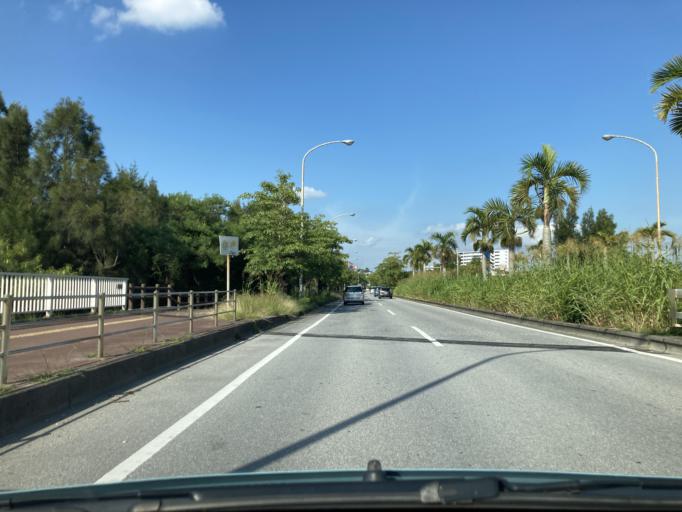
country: JP
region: Okinawa
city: Okinawa
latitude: 26.3032
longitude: 127.8148
